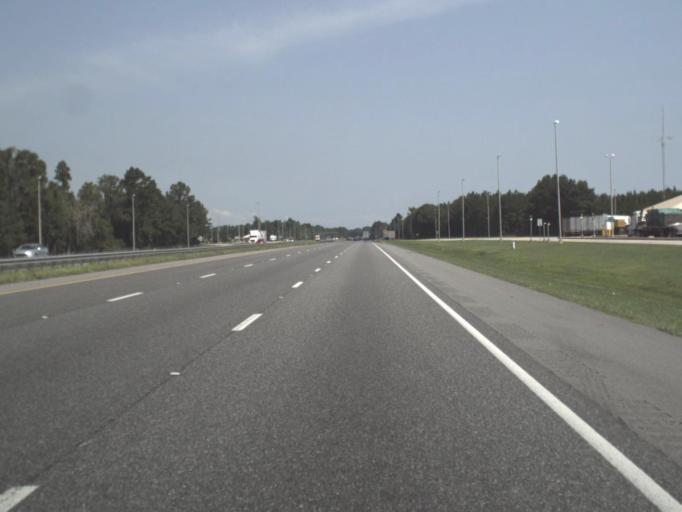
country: US
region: Florida
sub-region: Hamilton County
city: Jasper
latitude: 30.4168
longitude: -82.8981
